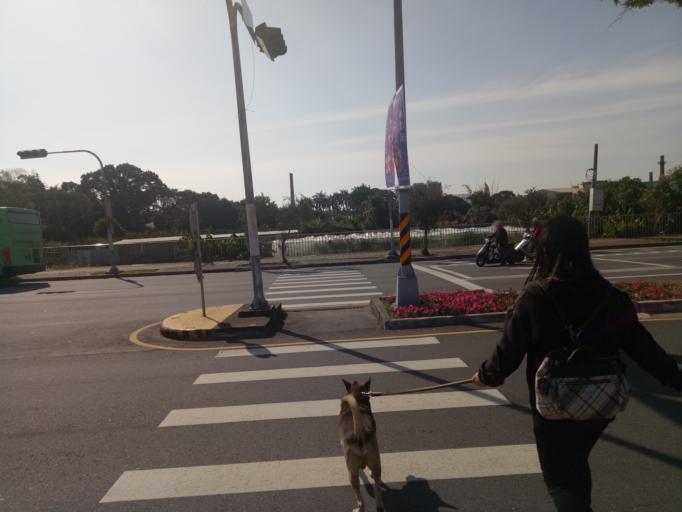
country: TW
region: Taiwan
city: Fengyuan
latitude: 24.2595
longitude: 120.7367
